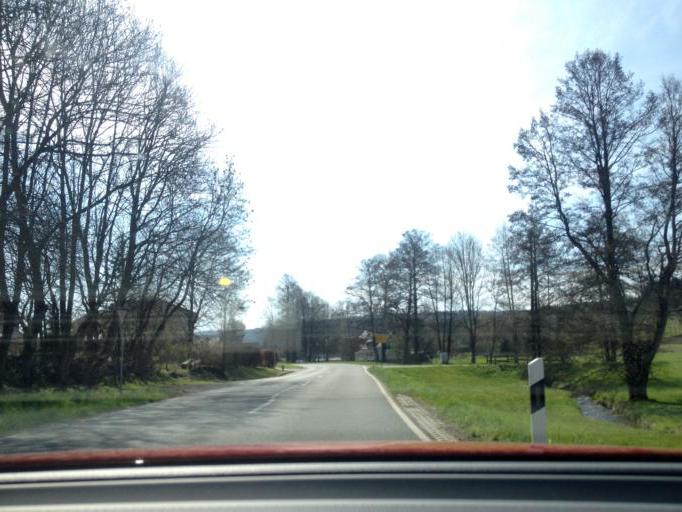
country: DE
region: Bavaria
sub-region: Upper Franconia
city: Oberhaid
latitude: 50.0973
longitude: 11.7869
